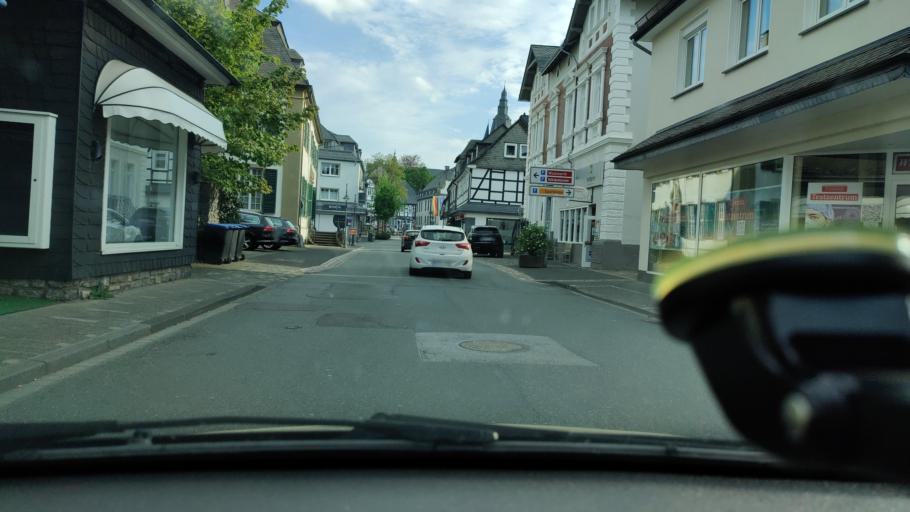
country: DE
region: North Rhine-Westphalia
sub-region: Regierungsbezirk Arnsberg
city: Brilon
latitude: 51.3968
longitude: 8.5683
